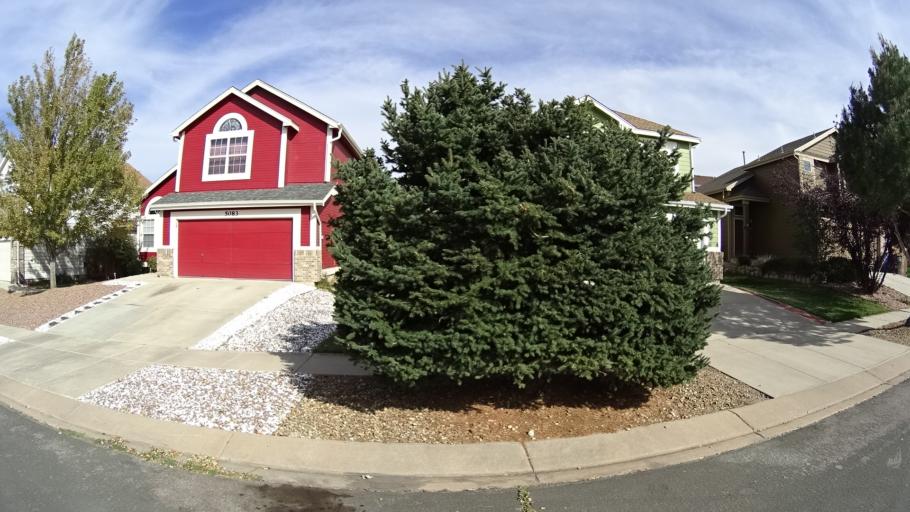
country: US
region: Colorado
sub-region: El Paso County
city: Cimarron Hills
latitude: 38.9060
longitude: -104.6939
